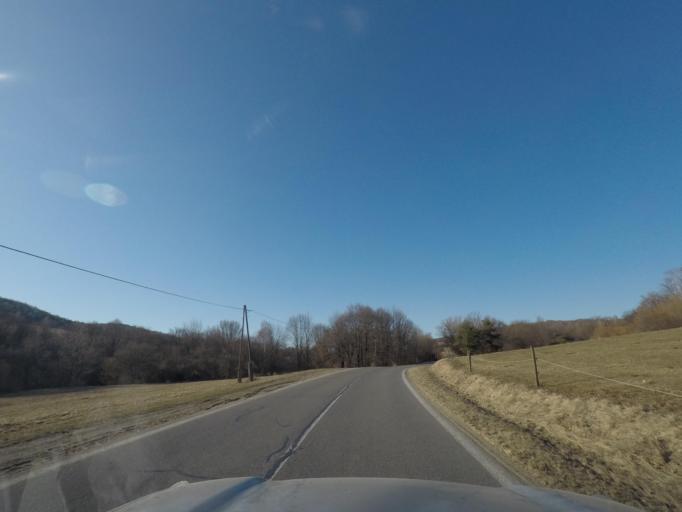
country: SK
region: Presovsky
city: Medzilaborce
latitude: 49.1821
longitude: 22.0145
